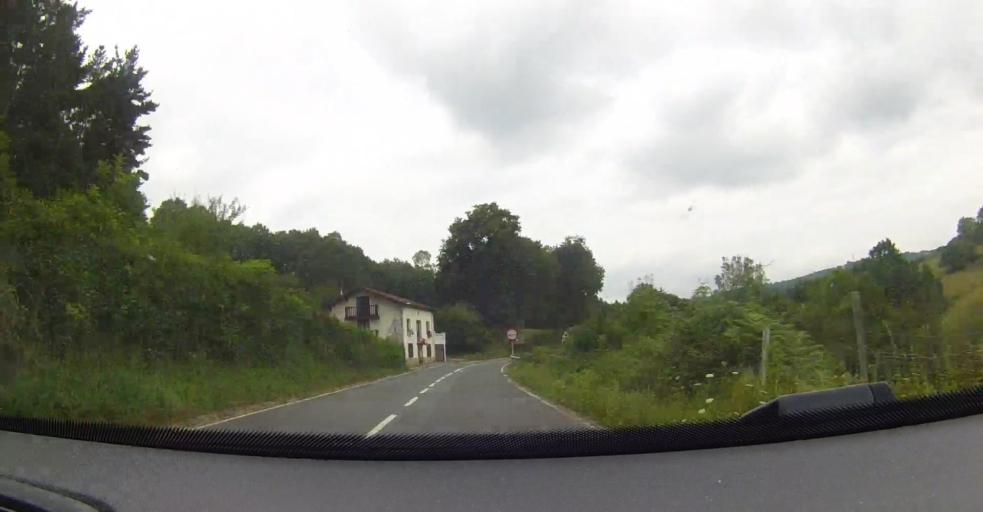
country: ES
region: Basque Country
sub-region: Bizkaia
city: Balmaseda
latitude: 43.2403
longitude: -3.2193
